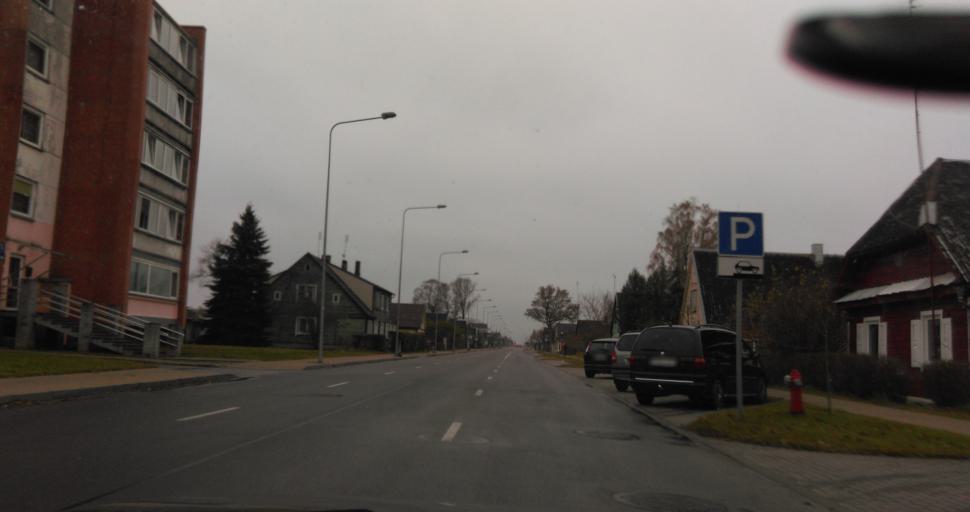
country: LT
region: Panevezys
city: Rokiskis
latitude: 55.9593
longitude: 25.5873
